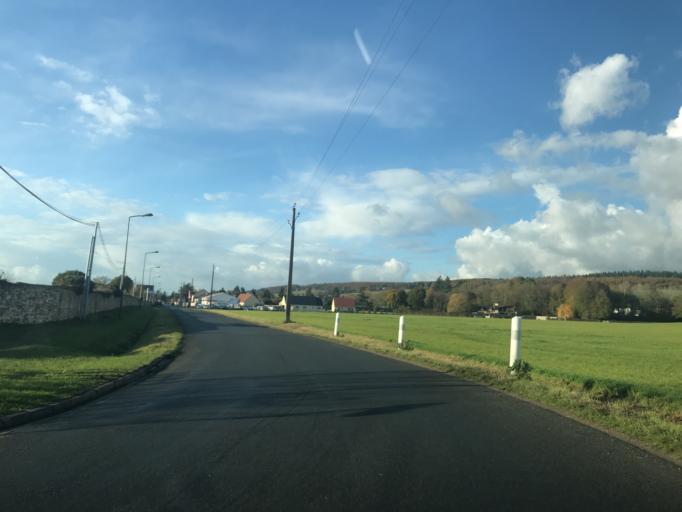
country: FR
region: Haute-Normandie
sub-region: Departement de l'Eure
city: Saint-Aubin-sur-Gaillon
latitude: 49.0929
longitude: 1.2861
